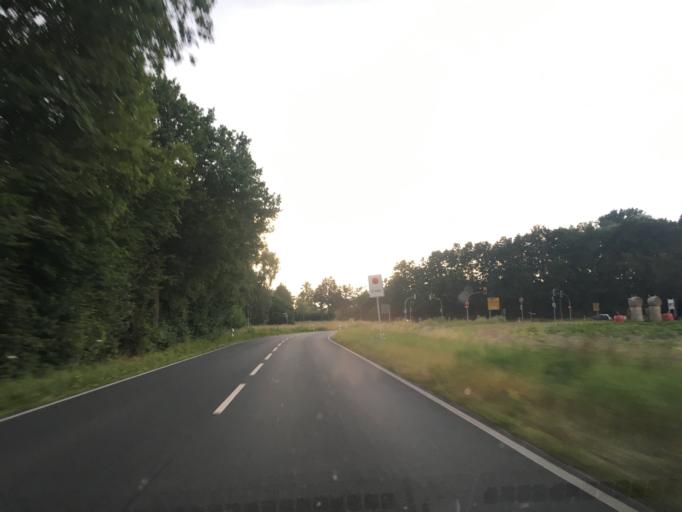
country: DE
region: North Rhine-Westphalia
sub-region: Regierungsbezirk Munster
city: Telgte
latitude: 51.9370
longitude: 7.7133
